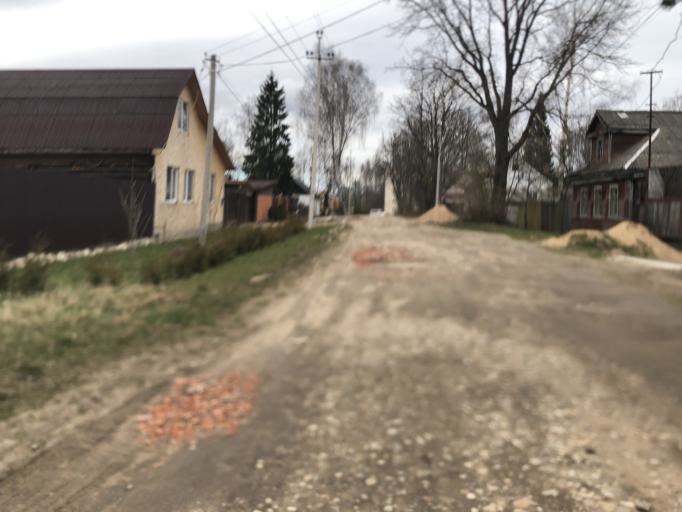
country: RU
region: Tverskaya
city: Rzhev
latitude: 56.2544
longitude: 34.3175
